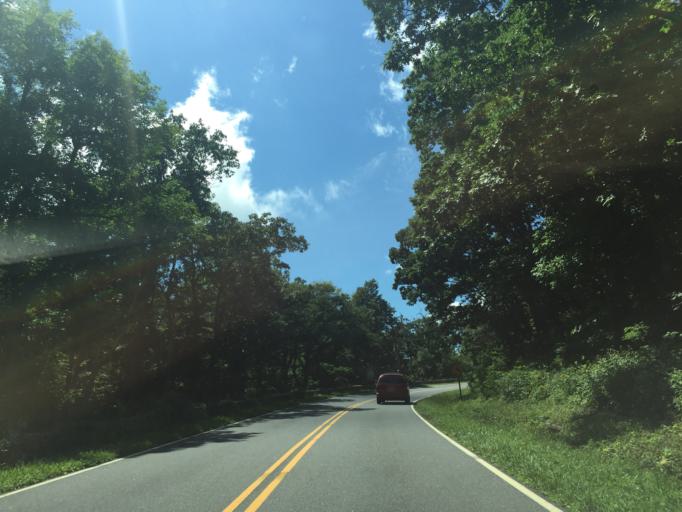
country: US
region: Virginia
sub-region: Rappahannock County
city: Washington
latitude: 38.7577
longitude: -78.2600
